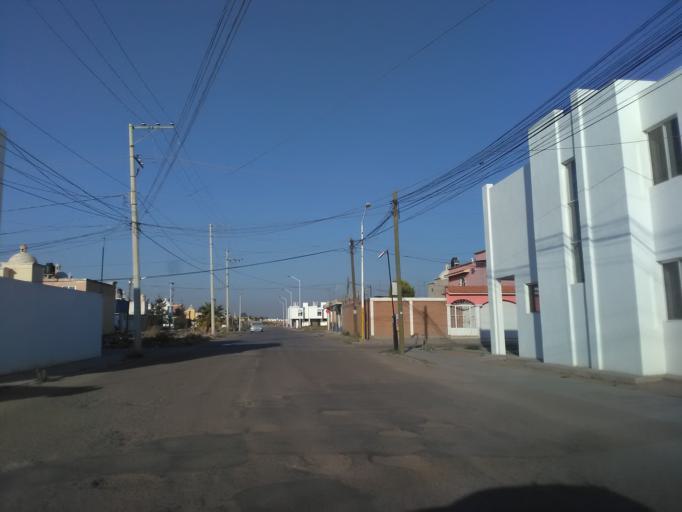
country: MX
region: Durango
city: Victoria de Durango
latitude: 24.0606
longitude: -104.6193
